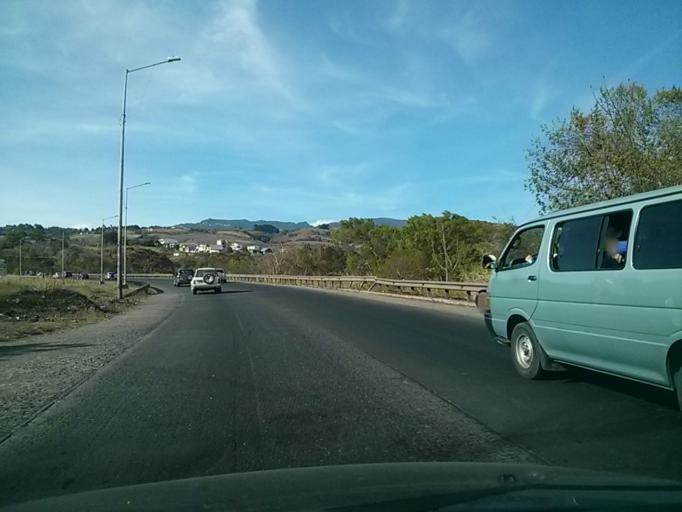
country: CR
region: Cartago
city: Cartago
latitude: 9.8863
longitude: -83.9348
